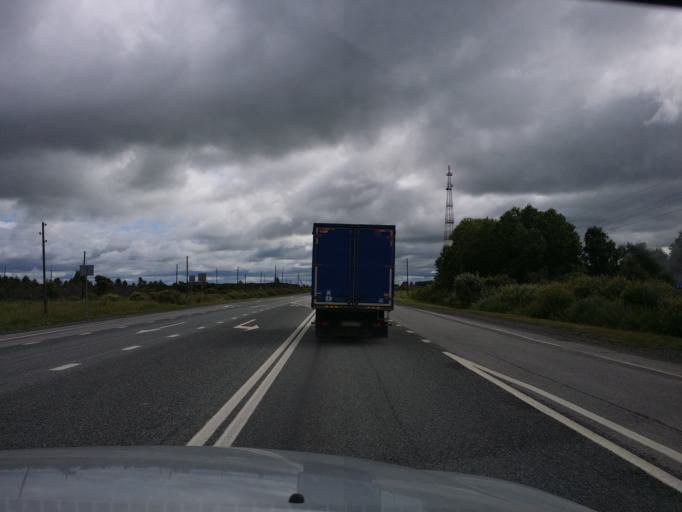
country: RU
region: Tjumen
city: Yarkovo
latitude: 57.2490
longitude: 66.7921
